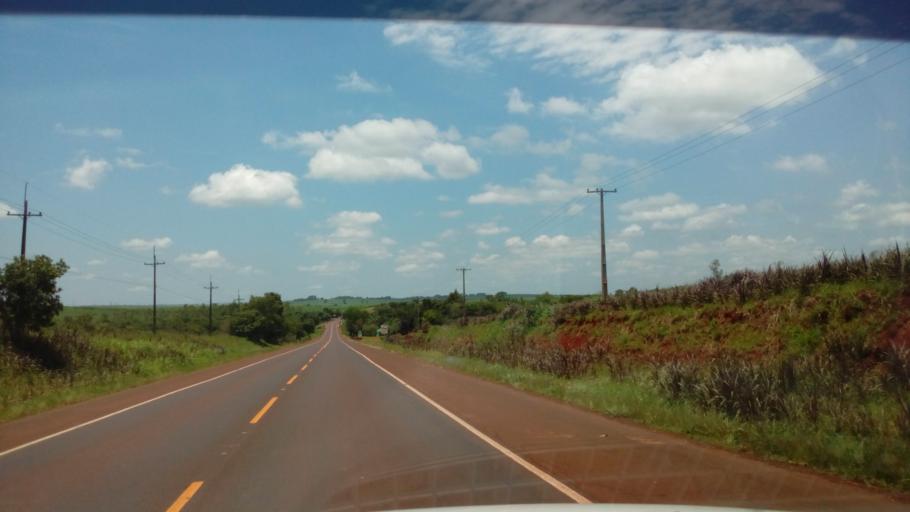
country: PY
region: Alto Parana
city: Naranjal
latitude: -26.0423
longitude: -55.1289
